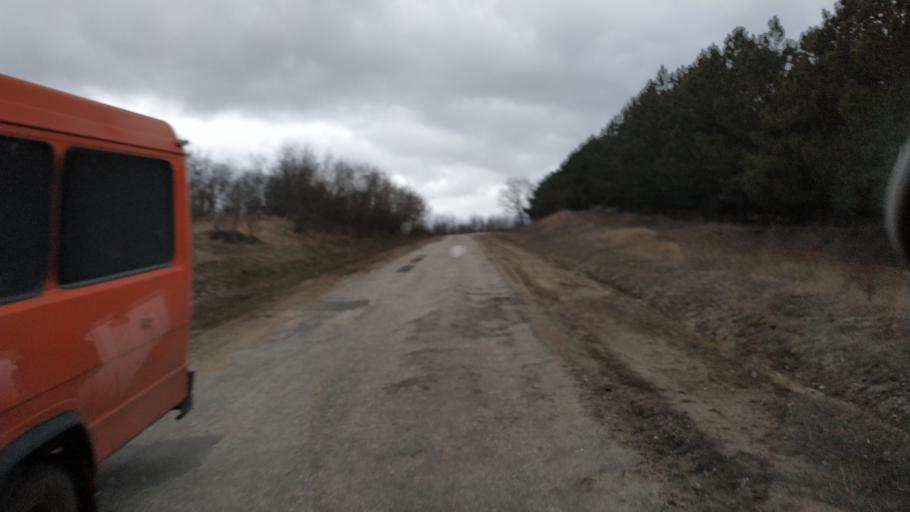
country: MD
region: Calarasi
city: Calarasi
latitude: 47.2219
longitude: 28.2613
